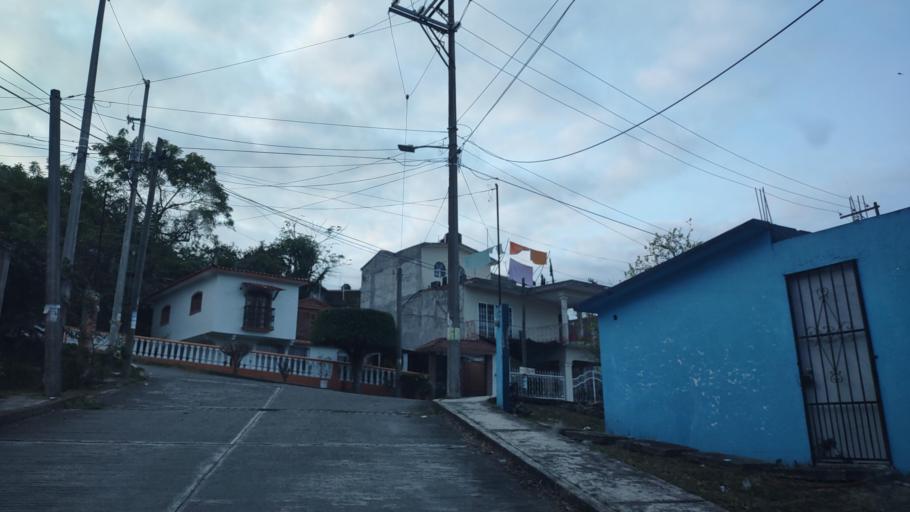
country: MX
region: Veracruz
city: Papantla de Olarte
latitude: 20.4618
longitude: -97.3064
